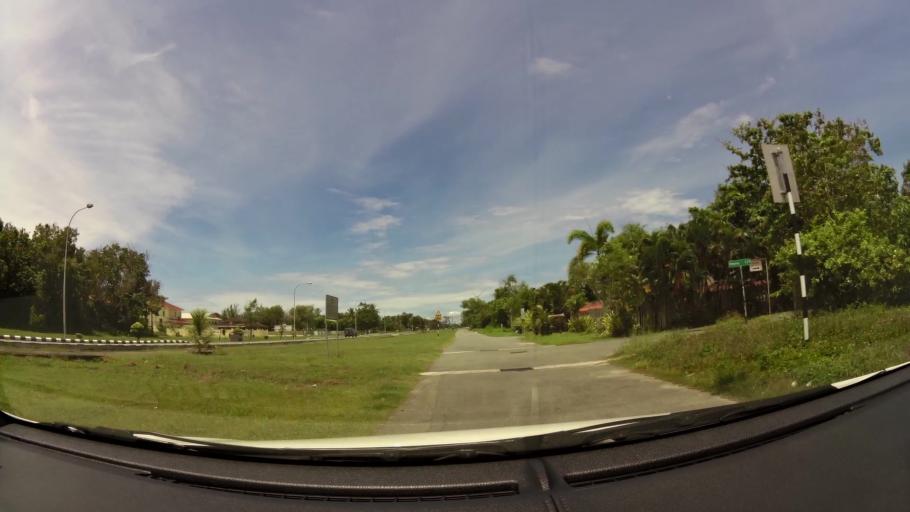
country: BN
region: Belait
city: Kuala Belait
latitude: 4.5931
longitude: 114.2340
